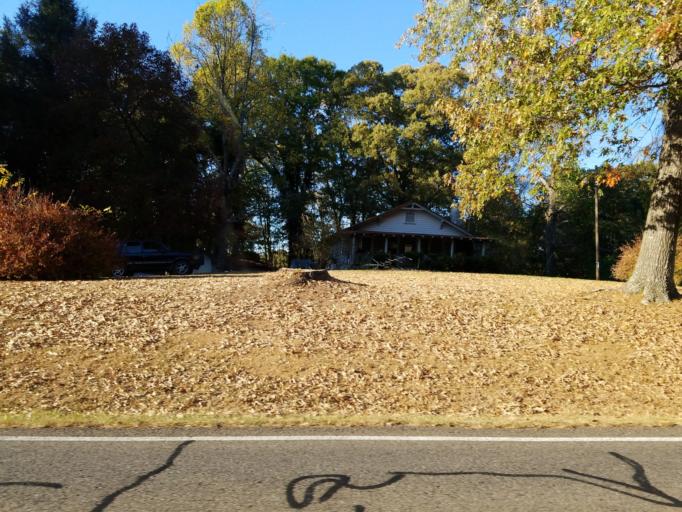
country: US
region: Georgia
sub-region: Gilmer County
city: Ellijay
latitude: 34.6510
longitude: -84.4295
